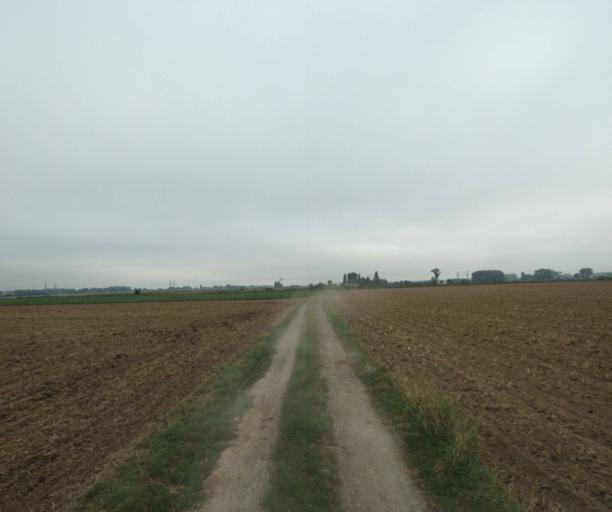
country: FR
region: Nord-Pas-de-Calais
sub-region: Departement du Nord
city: Baisieux
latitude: 50.6159
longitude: 3.2558
